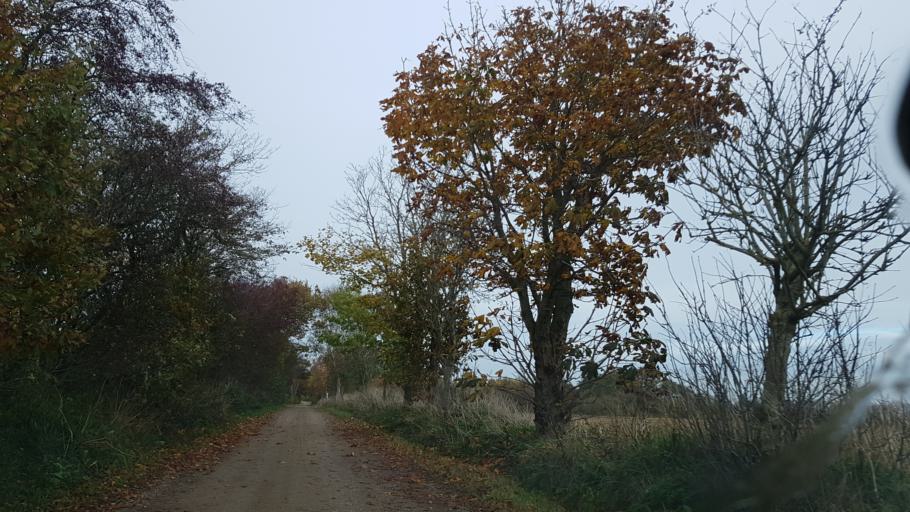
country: DK
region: South Denmark
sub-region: Tonder Kommune
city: Sherrebek
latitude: 55.2211
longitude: 8.8672
